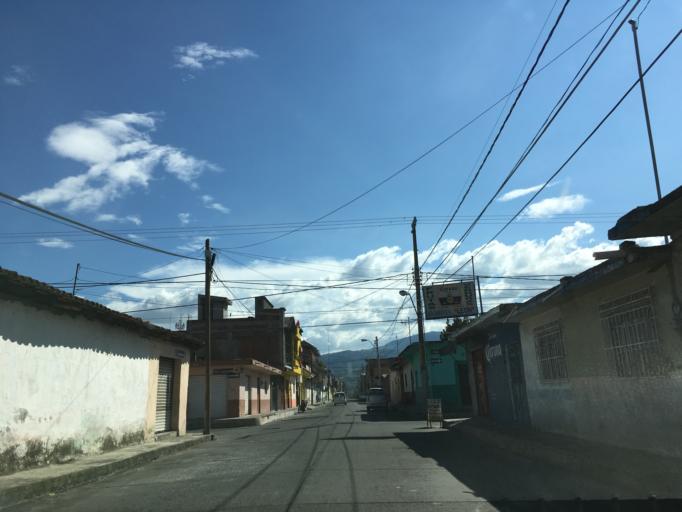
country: MX
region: Michoacan
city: Zacapu
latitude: 19.8200
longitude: -101.7833
